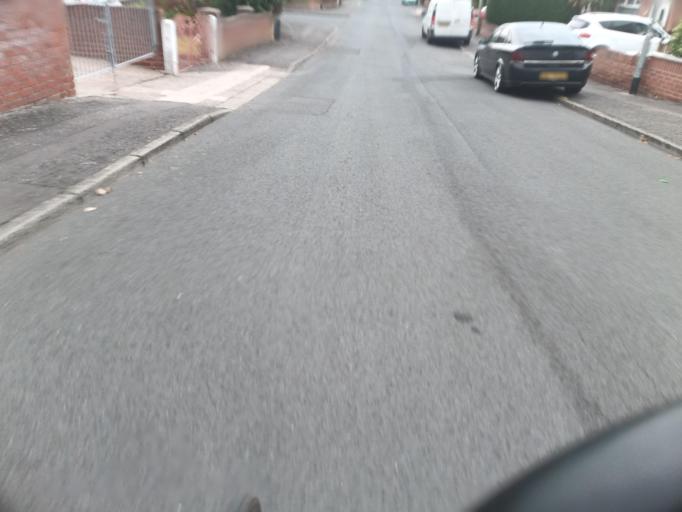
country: GB
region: Northern Ireland
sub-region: Ards District
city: Comber
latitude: 54.5573
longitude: -5.7323
